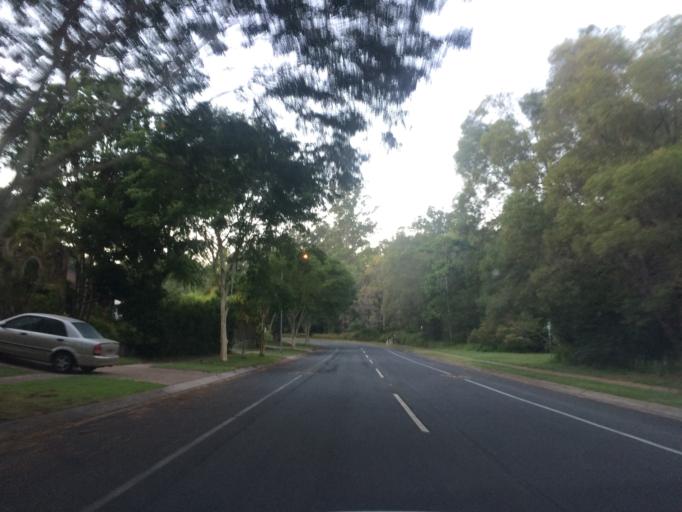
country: AU
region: Queensland
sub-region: Brisbane
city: Kenmore Hills
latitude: -27.4872
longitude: 152.9395
